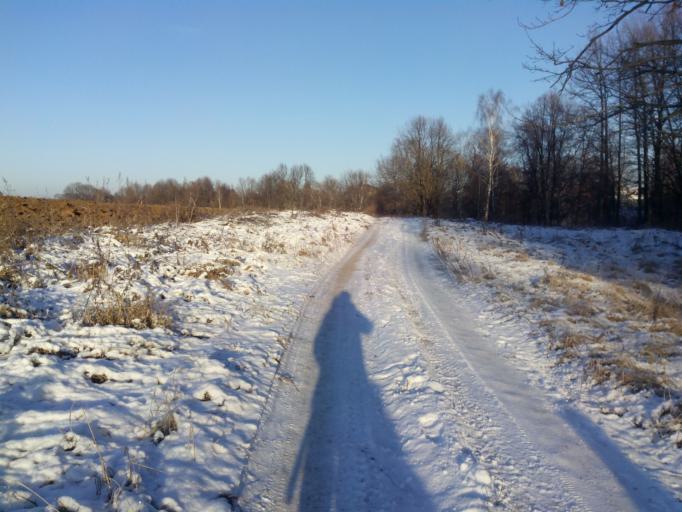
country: RU
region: Moskovskaya
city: Yakovlevskoye
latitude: 55.4931
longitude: 37.9525
